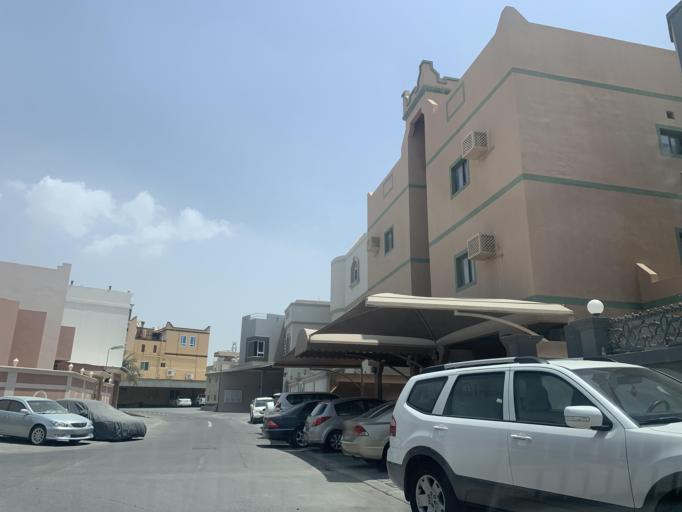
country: BH
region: Central Governorate
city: Madinat Hamad
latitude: 26.1444
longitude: 50.4954
